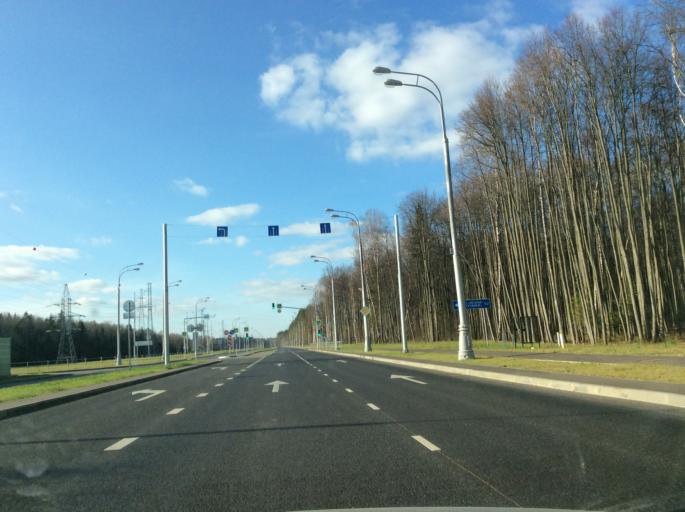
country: RU
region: Moskovskaya
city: Vatutinki
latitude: 55.4830
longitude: 37.3572
